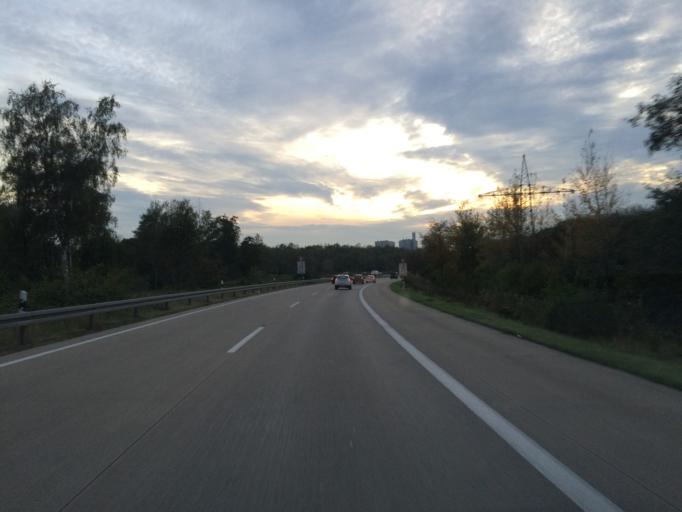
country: DE
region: Lower Saxony
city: Garbsen-Mitte
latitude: 52.4285
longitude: 9.6661
